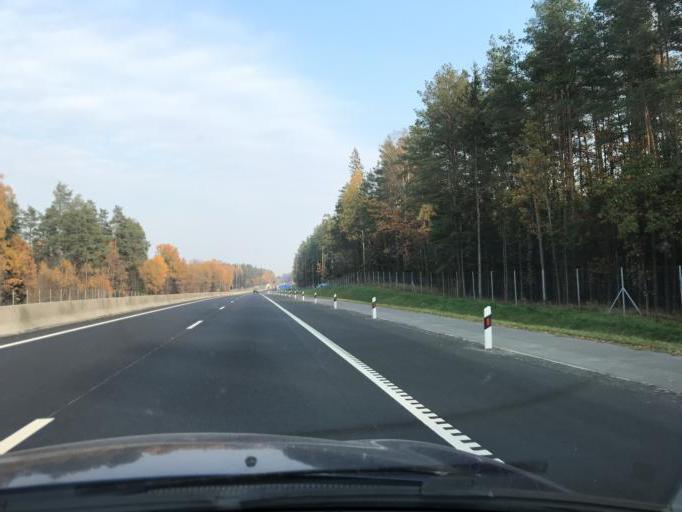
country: BY
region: Grodnenskaya
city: Shchuchin
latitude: 53.6626
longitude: 24.8149
